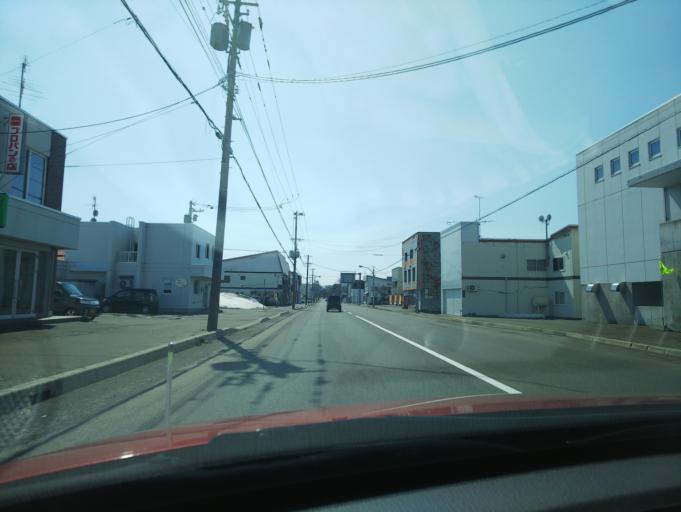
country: JP
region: Hokkaido
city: Nayoro
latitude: 44.2928
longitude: 142.4202
